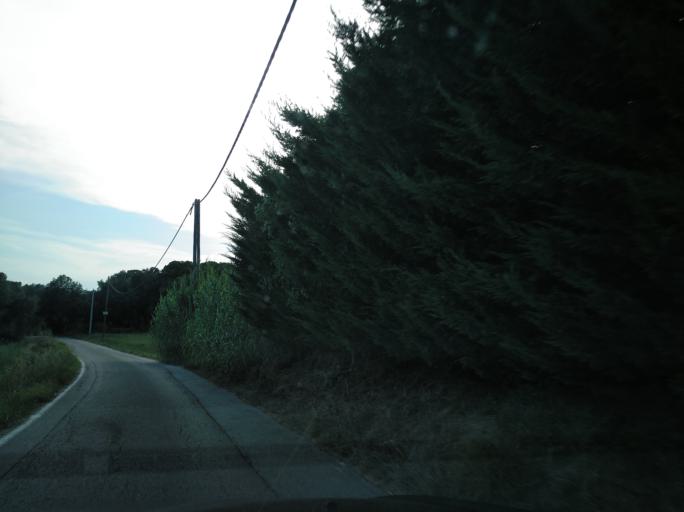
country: ES
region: Catalonia
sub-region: Provincia de Girona
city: Aiguaviva
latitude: 41.9409
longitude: 2.7705
